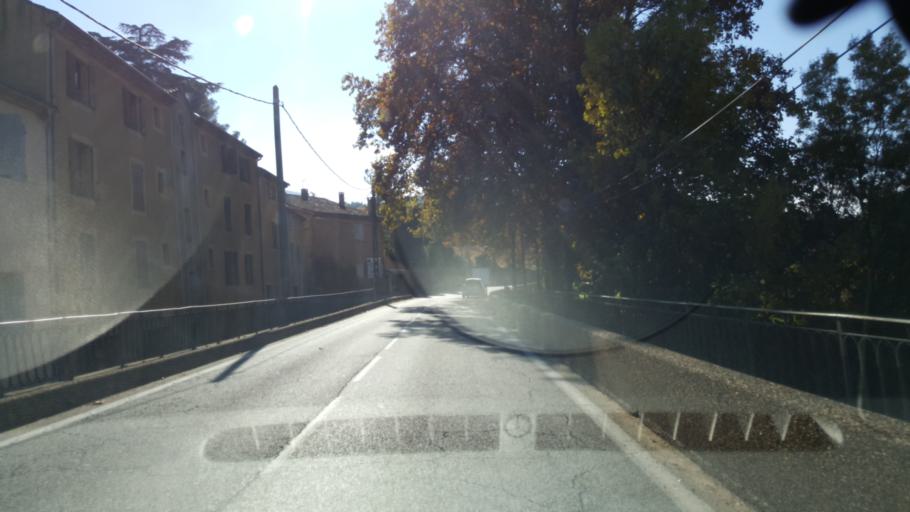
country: FR
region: Provence-Alpes-Cote d'Azur
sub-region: Departement du Var
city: Saint-Zacharie
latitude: 43.3802
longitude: 5.6996
